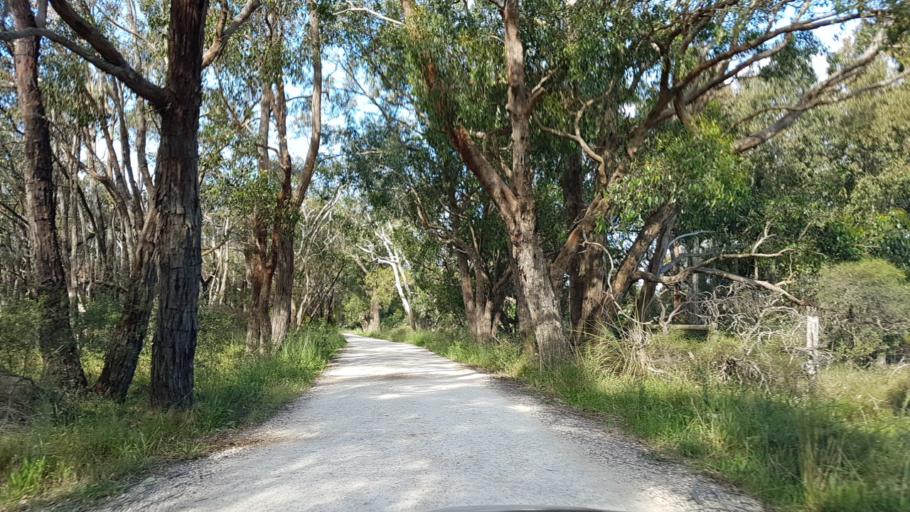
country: AU
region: South Australia
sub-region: Adelaide Hills
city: Adelaide Hills
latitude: -34.9063
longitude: 138.7390
